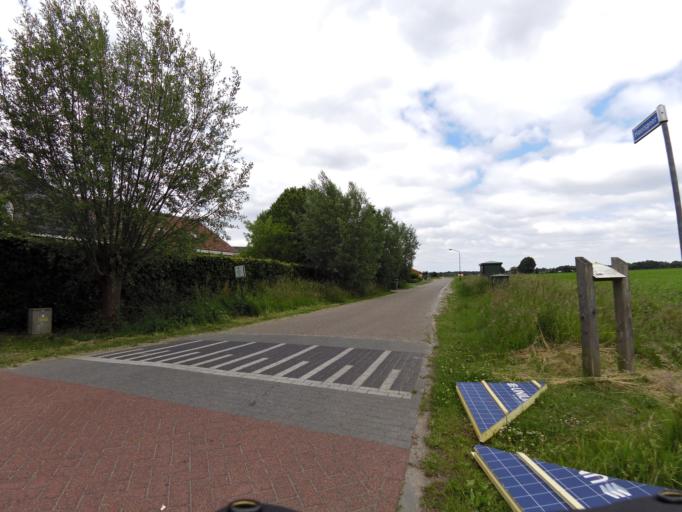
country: NL
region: North Brabant
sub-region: Gemeente Baarle-Nassau
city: Baarle-Nassau
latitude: 51.4763
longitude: 4.9397
